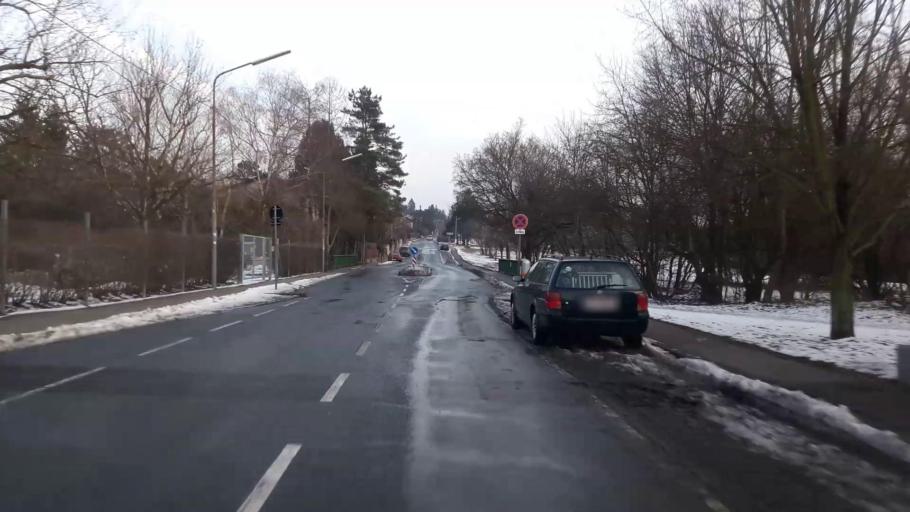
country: AT
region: Lower Austria
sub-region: Politischer Bezirk Wien-Umgebung
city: Purkersdorf
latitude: 48.2128
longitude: 16.2286
